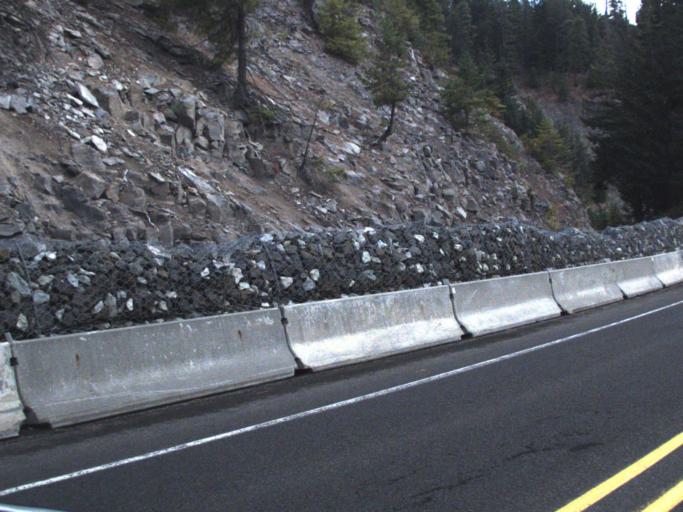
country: US
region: Washington
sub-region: Yakima County
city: Tieton
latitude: 46.6528
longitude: -121.2984
